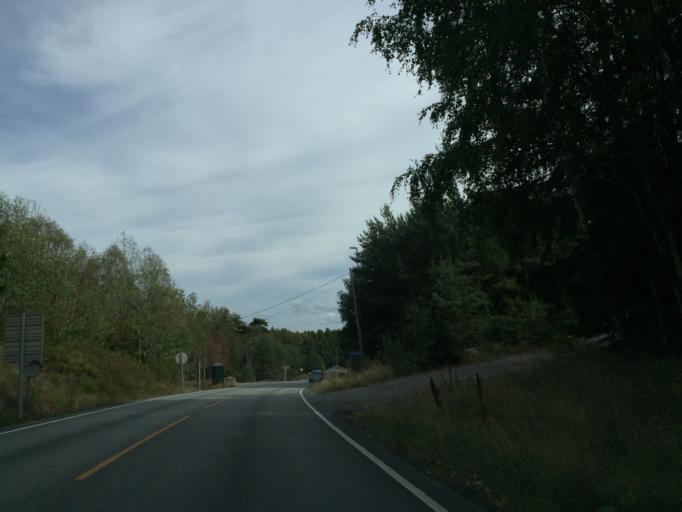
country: NO
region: Ostfold
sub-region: Hvaler
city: Skjaerhalden
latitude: 59.0377
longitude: 11.0054
